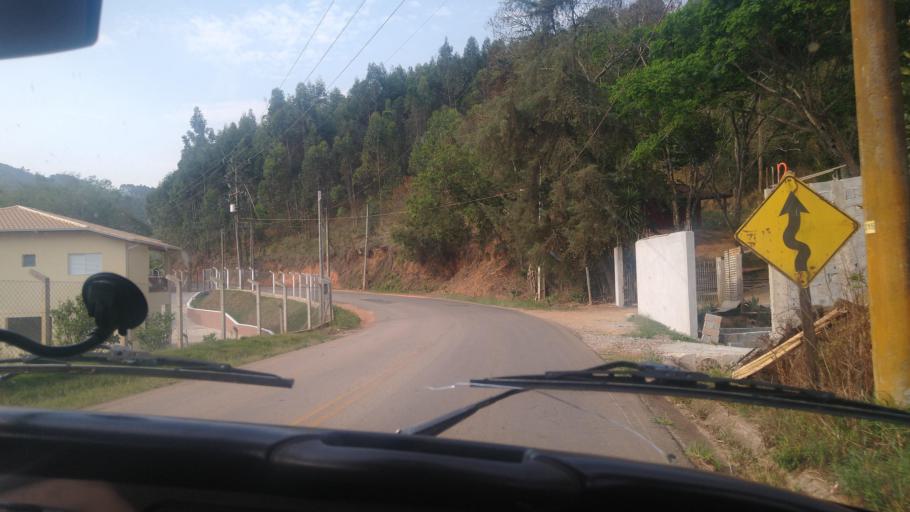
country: BR
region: Minas Gerais
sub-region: Extrema
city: Extrema
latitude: -22.7778
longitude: -46.4404
